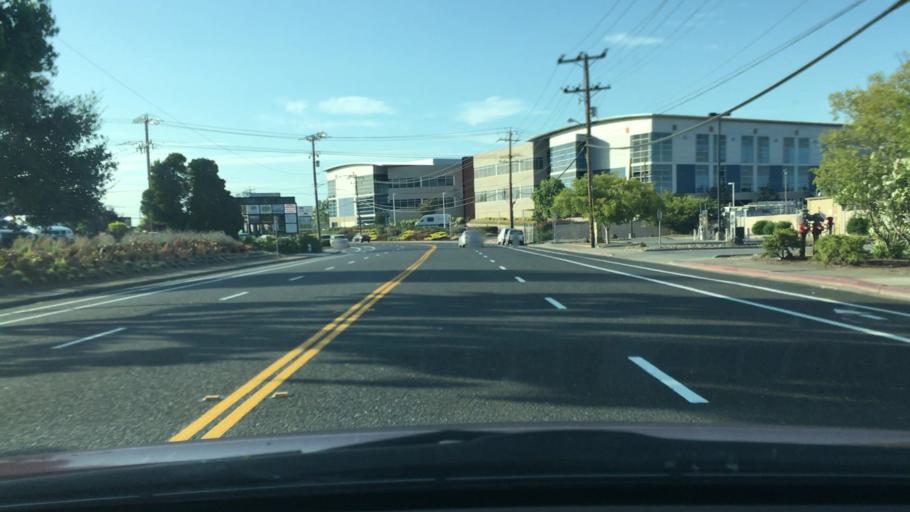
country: US
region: California
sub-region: San Mateo County
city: San Carlos
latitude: 37.5174
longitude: -122.2636
